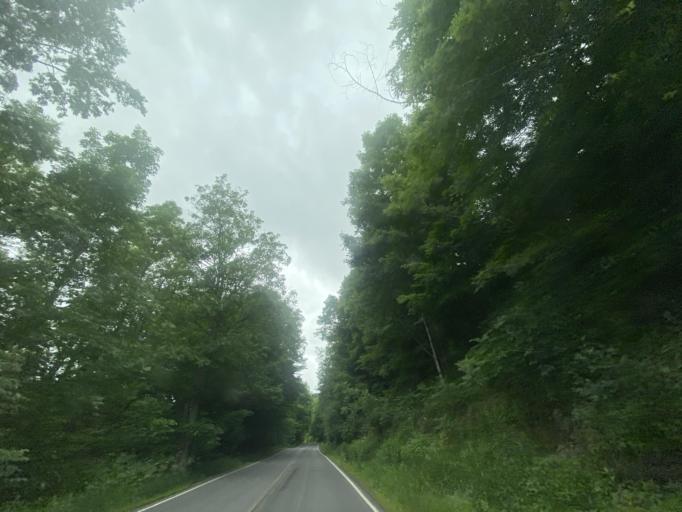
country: US
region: New York
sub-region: Schoharie County
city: Middleburgh
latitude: 42.3901
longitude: -74.3389
